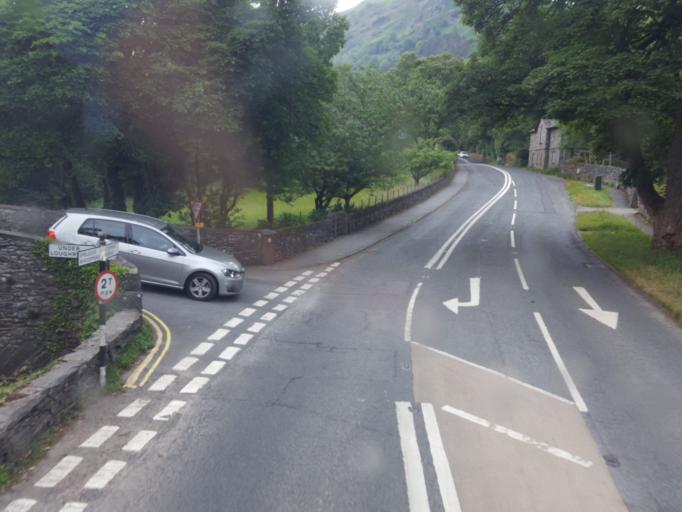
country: GB
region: England
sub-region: Cumbria
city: Ambleside
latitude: 54.4451
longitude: -2.9785
